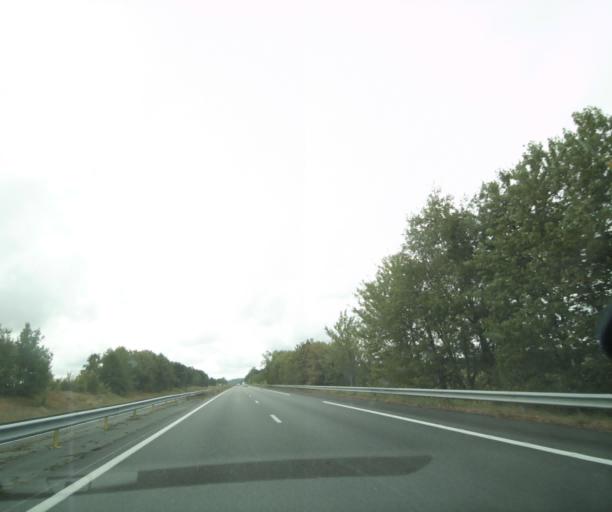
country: FR
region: Poitou-Charentes
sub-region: Departement de la Charente-Maritime
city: Saint-Genis-de-Saintonge
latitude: 45.4337
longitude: -0.6056
